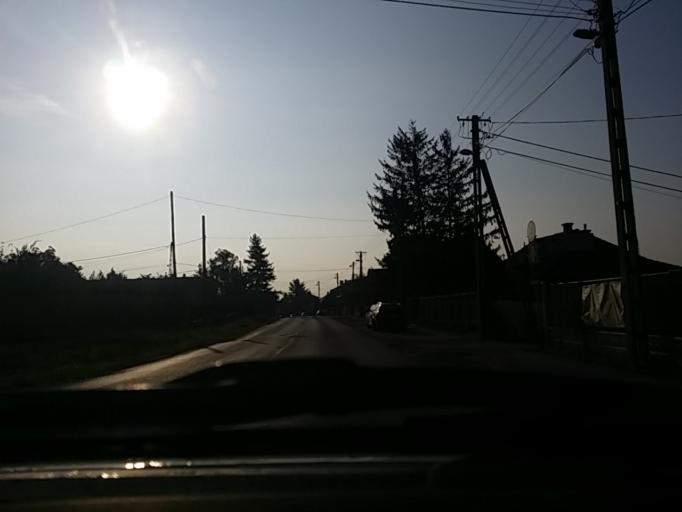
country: HU
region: Pest
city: Szentendre
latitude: 47.6728
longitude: 19.0680
